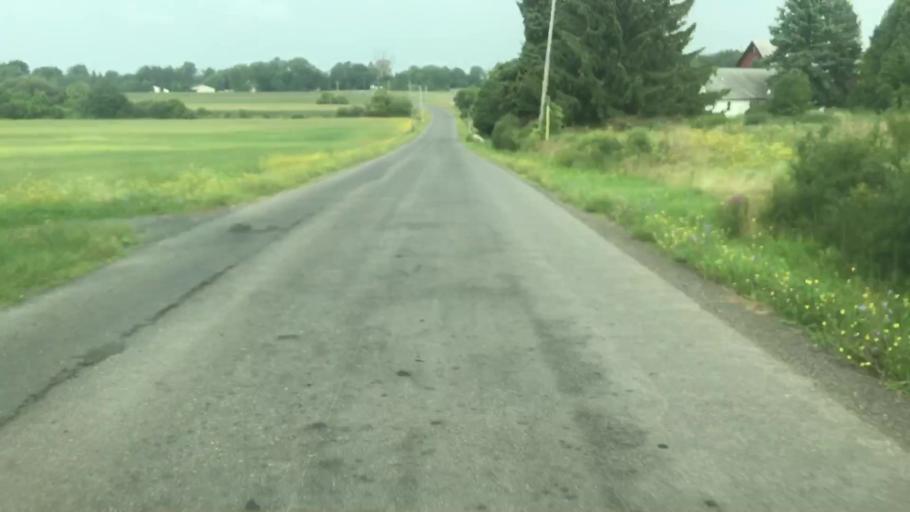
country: US
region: New York
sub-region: Onondaga County
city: Skaneateles
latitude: 42.9026
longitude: -76.4602
